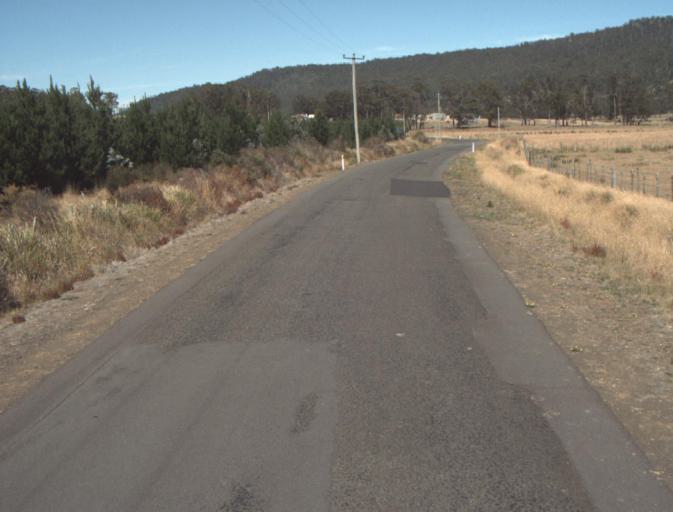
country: AU
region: Tasmania
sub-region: Launceston
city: Newstead
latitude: -41.3307
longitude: 147.3089
